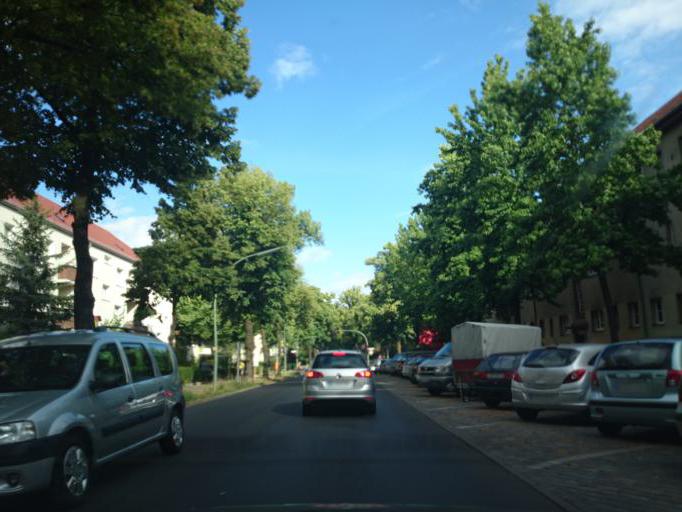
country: DE
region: Berlin
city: Lankwitz
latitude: 52.4346
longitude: 13.3491
